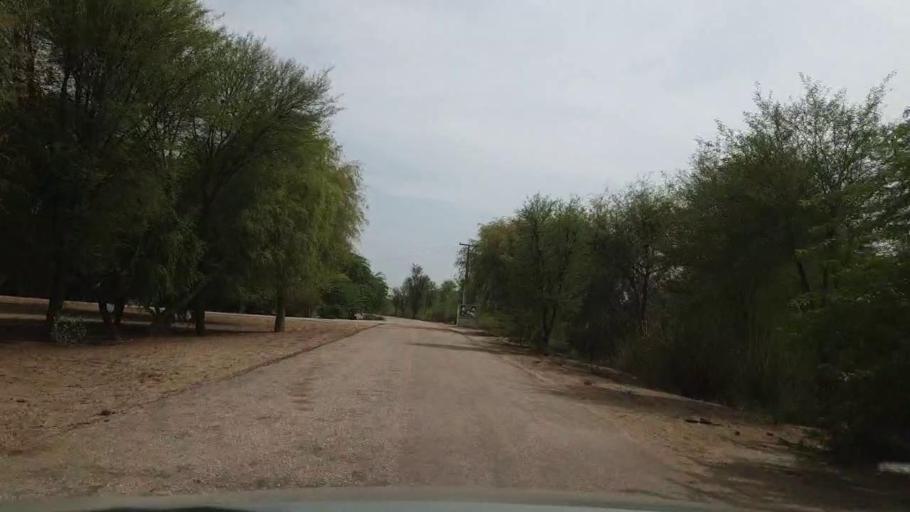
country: PK
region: Sindh
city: Bozdar
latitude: 27.0830
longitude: 69.0138
